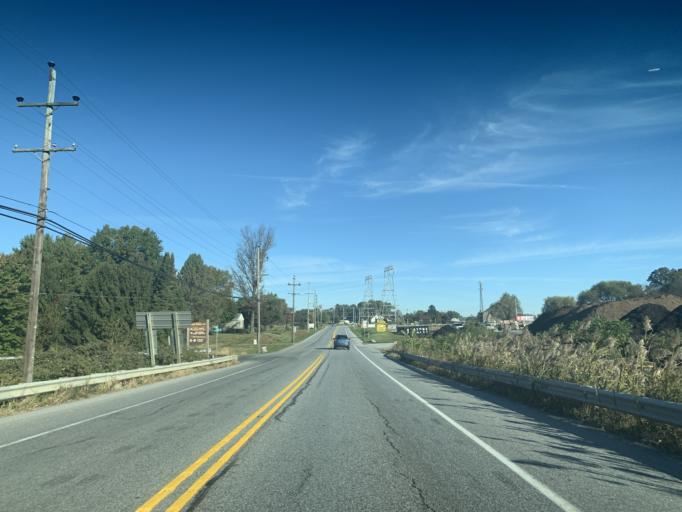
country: US
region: Pennsylvania
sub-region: Chester County
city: Oxford
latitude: 39.8089
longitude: -75.9673
